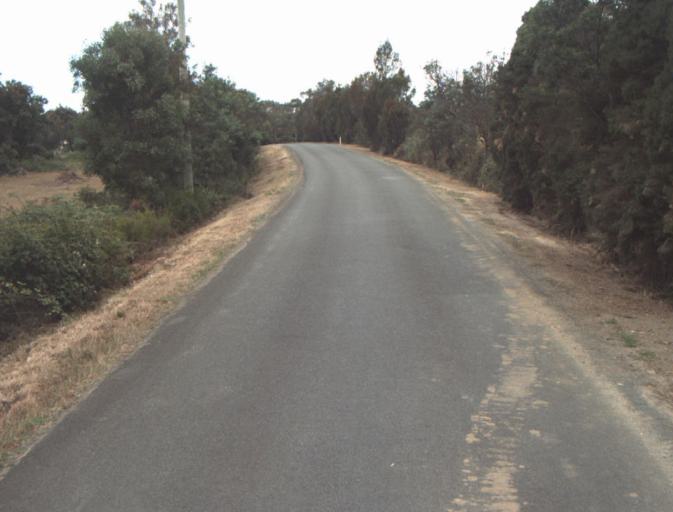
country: AU
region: Tasmania
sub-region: Launceston
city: Mayfield
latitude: -41.2282
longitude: 147.0275
